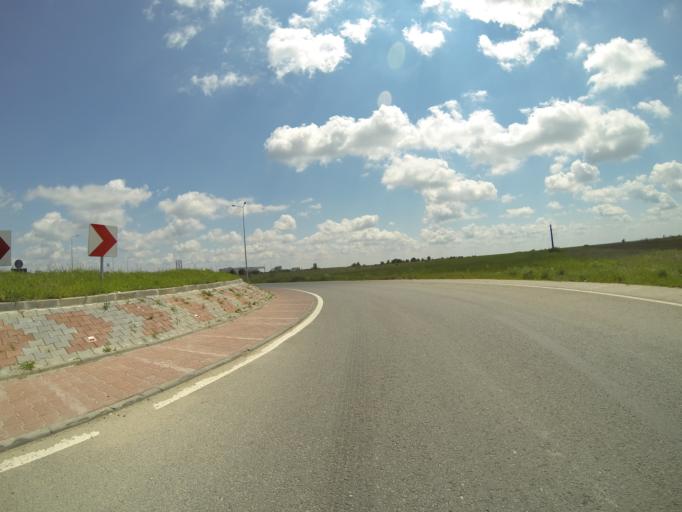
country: RO
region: Dolj
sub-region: Comuna Carcea
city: Carcea
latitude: 44.2609
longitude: 23.9058
